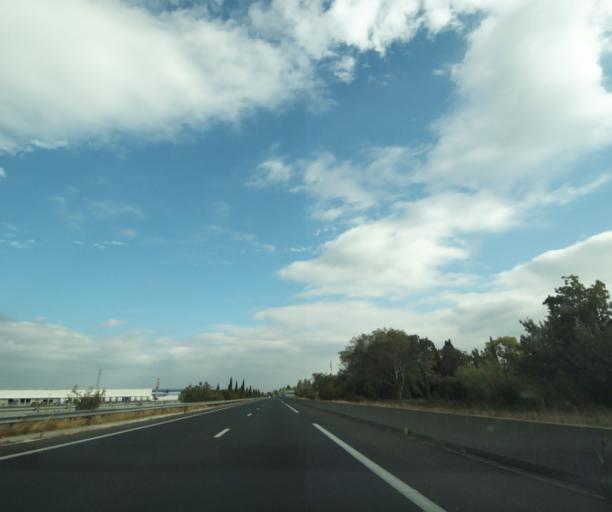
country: FR
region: Provence-Alpes-Cote d'Azur
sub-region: Departement des Bouches-du-Rhone
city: Grans
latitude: 43.6355
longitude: 5.0351
